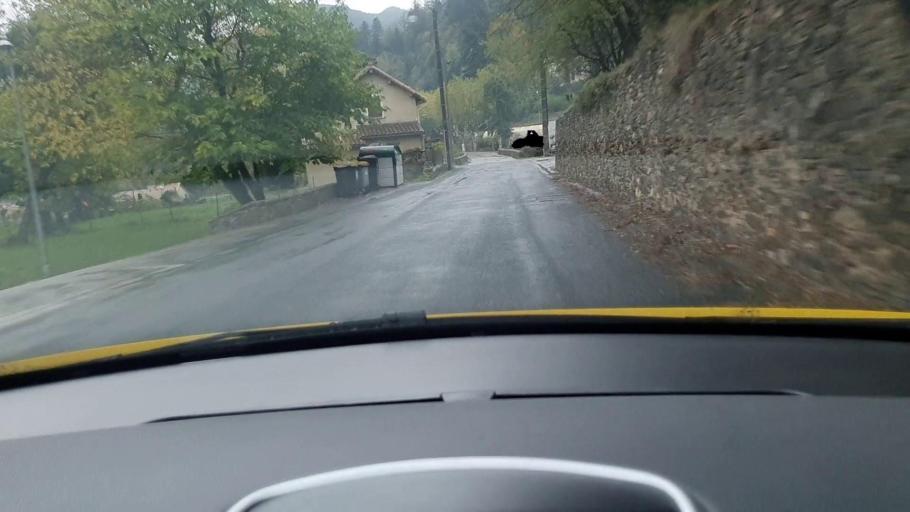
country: FR
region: Languedoc-Roussillon
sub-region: Departement du Gard
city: Sumene
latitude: 43.9856
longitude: 3.7141
